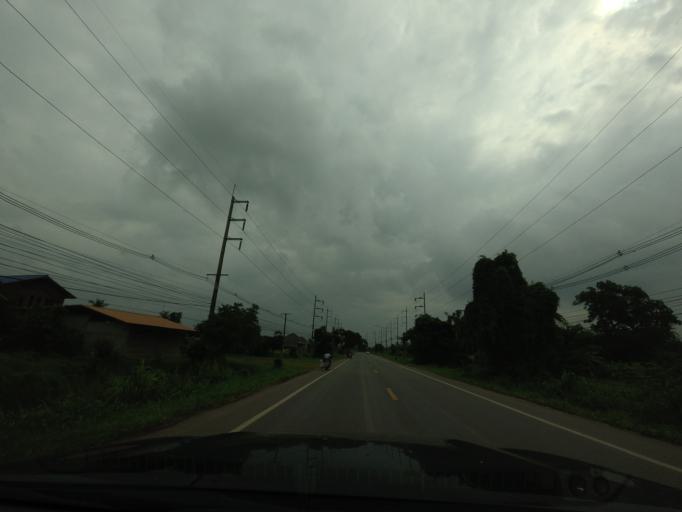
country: TH
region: Nong Khai
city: Tha Bo
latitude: 17.8924
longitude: 102.5979
